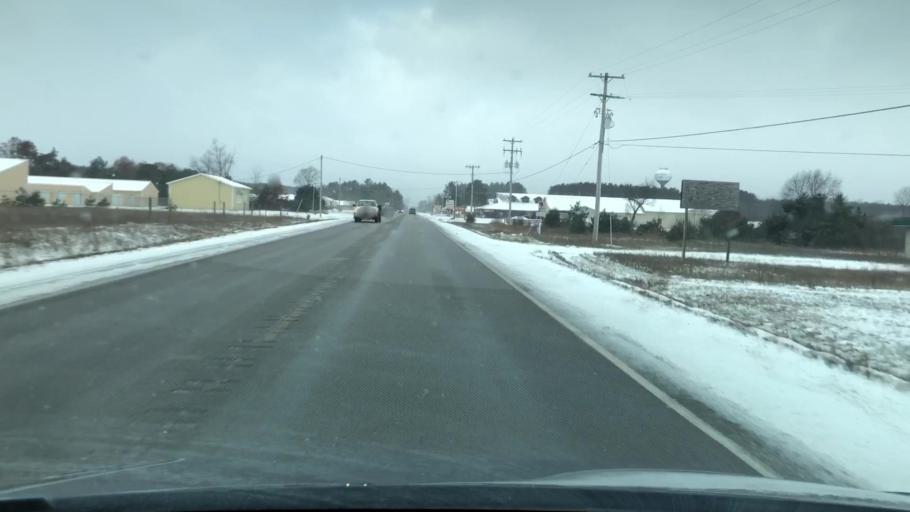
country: US
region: Michigan
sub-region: Wexford County
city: Cadillac
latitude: 44.2813
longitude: -85.4298
